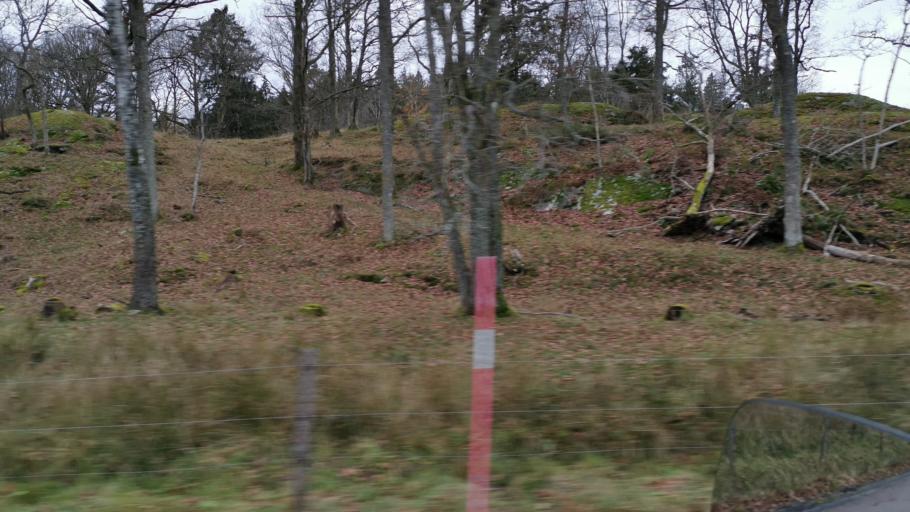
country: SE
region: Vaestra Goetaland
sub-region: Orust
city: Henan
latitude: 58.2073
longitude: 11.7353
